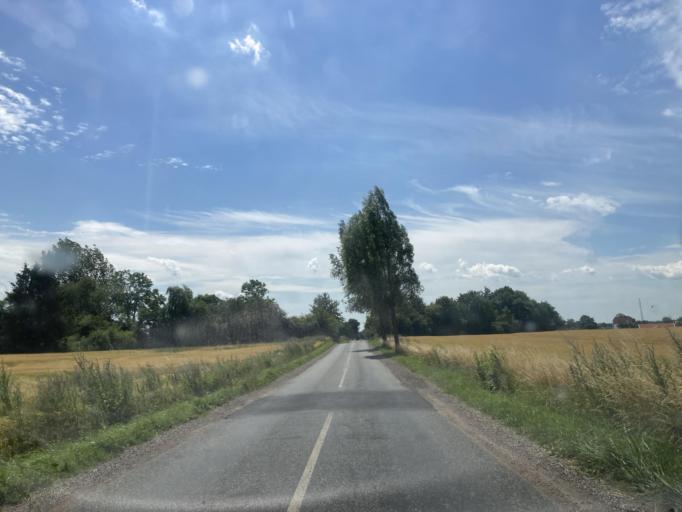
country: DK
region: Zealand
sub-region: Faxe Kommune
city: Haslev
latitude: 55.3949
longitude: 11.9403
